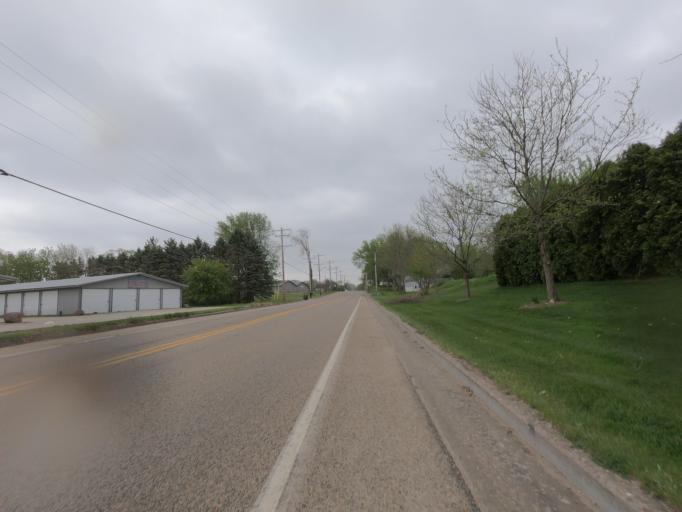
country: US
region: Wisconsin
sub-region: Jefferson County
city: Jefferson
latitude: 43.0165
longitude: -88.8097
